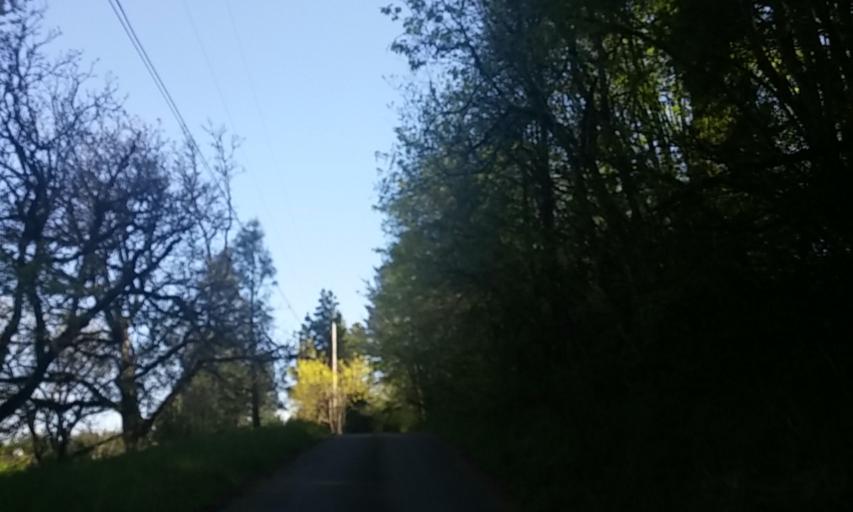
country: US
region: Oregon
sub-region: Washington County
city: Cedar Mill
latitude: 45.5492
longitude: -122.7884
